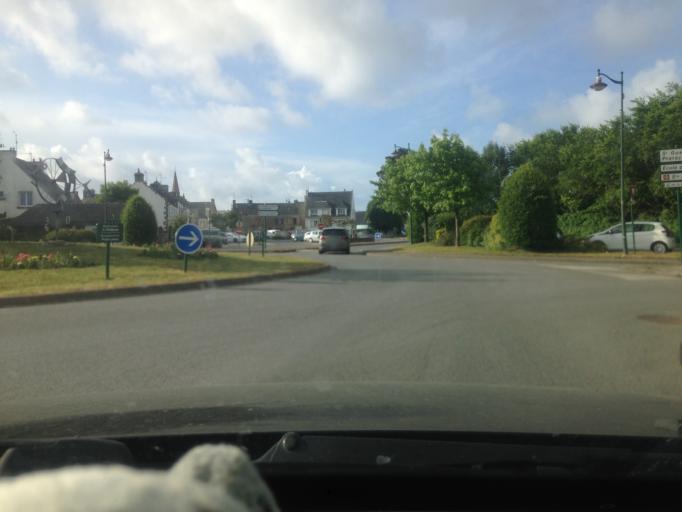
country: FR
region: Brittany
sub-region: Departement du Morbihan
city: Plouharnel
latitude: 47.5997
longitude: -3.1152
